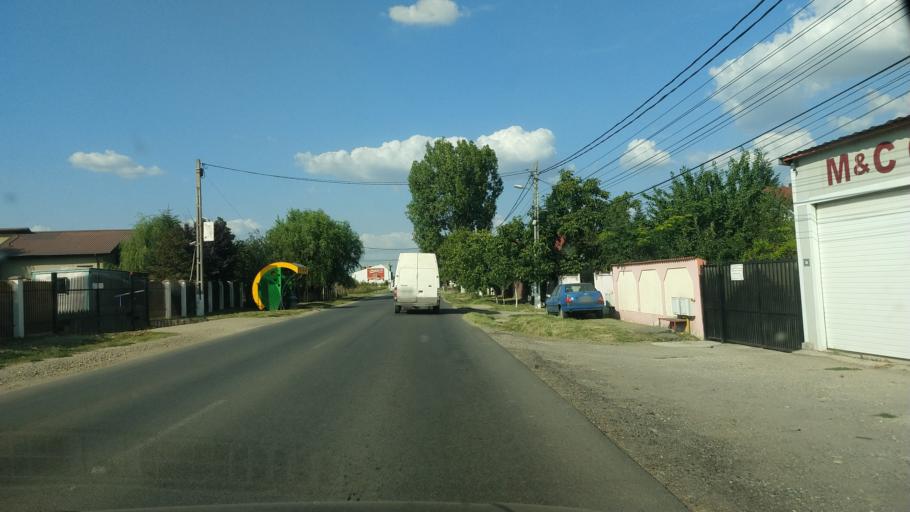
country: RO
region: Ilfov
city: Stefanestii de Jos
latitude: 44.5241
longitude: 26.1965
